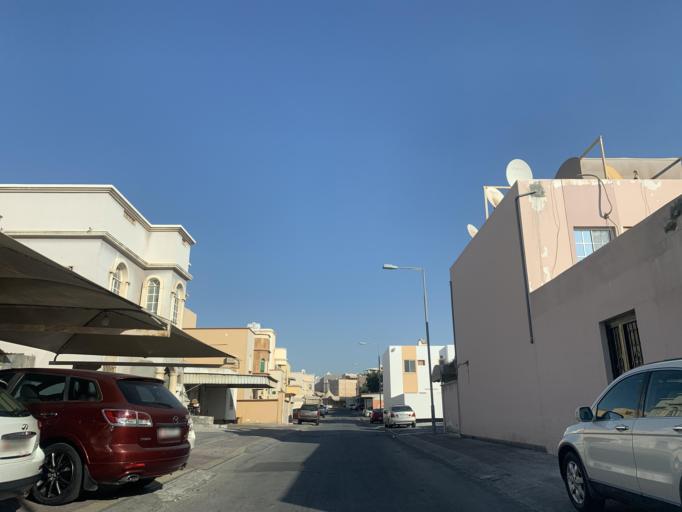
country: BH
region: Central Governorate
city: Madinat Hamad
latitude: 26.1092
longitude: 50.5058
